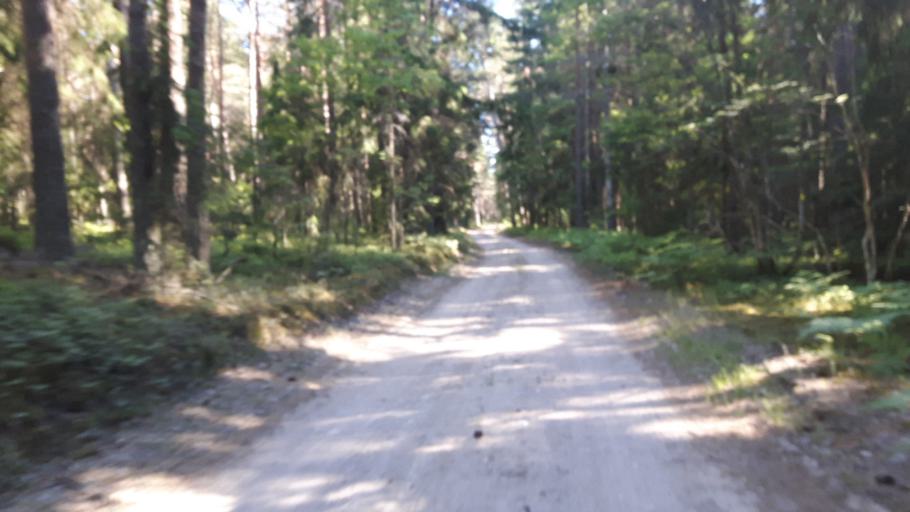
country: LV
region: Salacgrivas
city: Salacgriva
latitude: 57.7333
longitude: 24.3500
